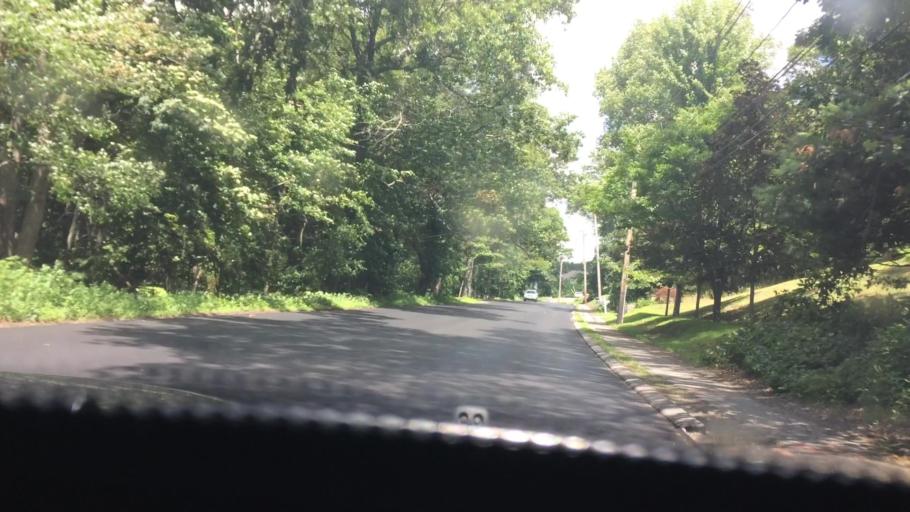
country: US
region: Massachusetts
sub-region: Middlesex County
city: Sudbury
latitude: 42.4024
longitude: -71.4361
